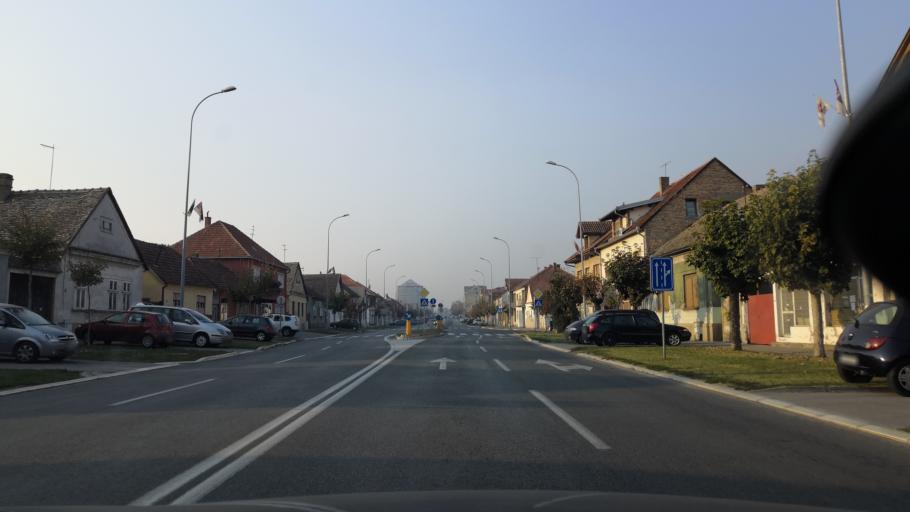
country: RS
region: Autonomna Pokrajina Vojvodina
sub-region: Sremski Okrug
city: Ingija
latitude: 45.0433
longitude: 20.0855
